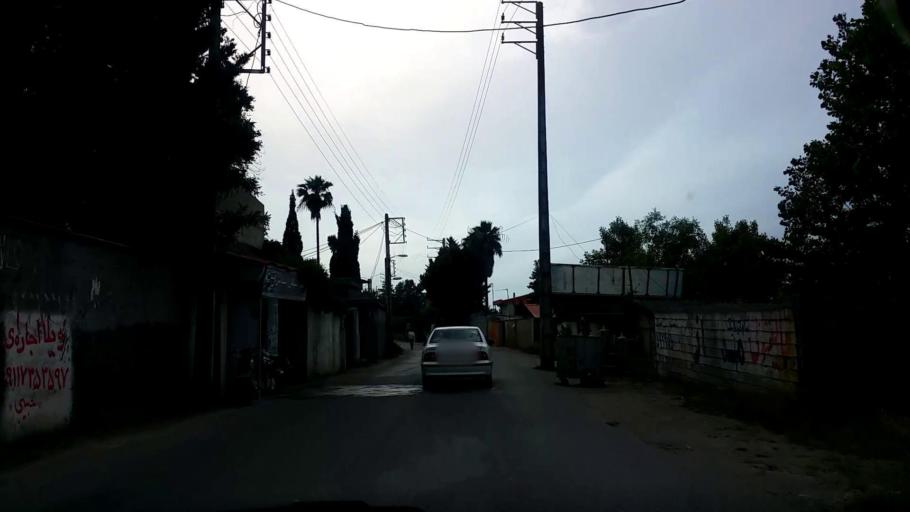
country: IR
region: Mazandaran
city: Chalus
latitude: 36.6862
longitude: 51.4097
